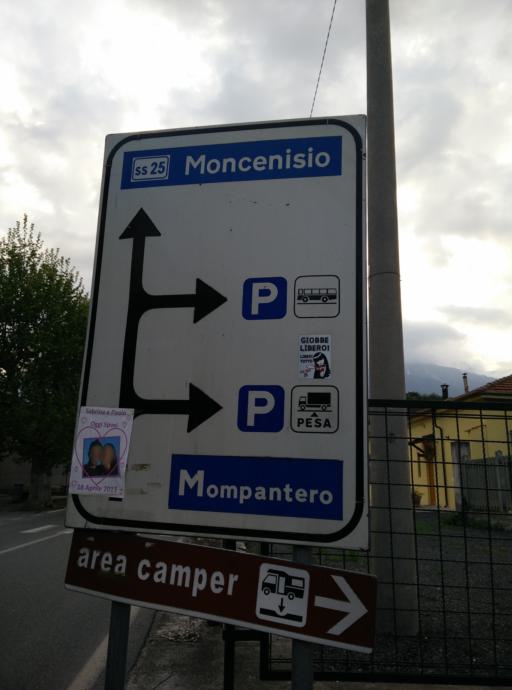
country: IT
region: Piedmont
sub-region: Provincia di Torino
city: Susa
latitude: 45.1379
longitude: 7.0534
